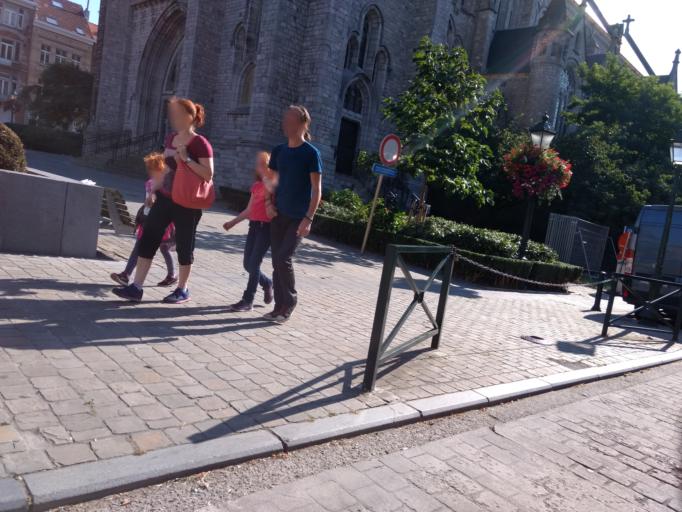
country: BE
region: Brussels Capital
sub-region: Bruxelles-Capitale
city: Brussels
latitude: 50.8297
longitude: 4.3859
